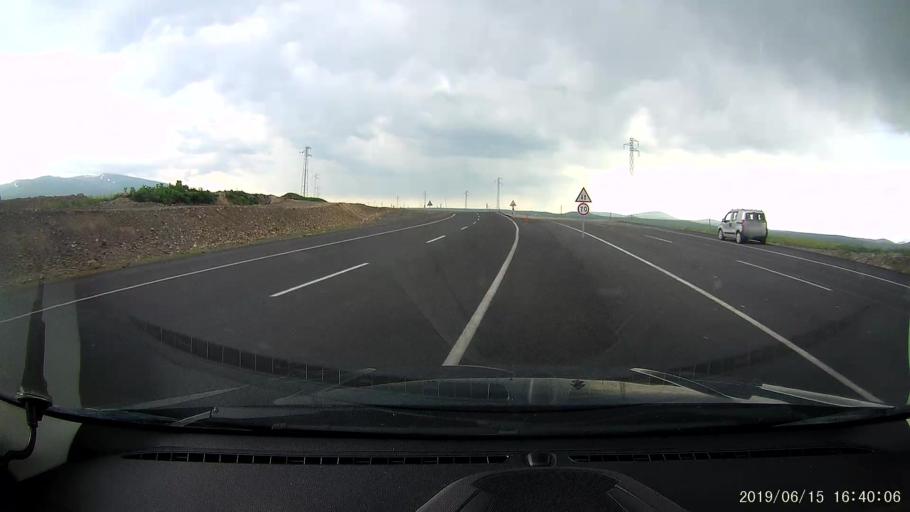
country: TR
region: Ardahan
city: Haskoy
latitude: 40.9736
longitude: 42.8940
